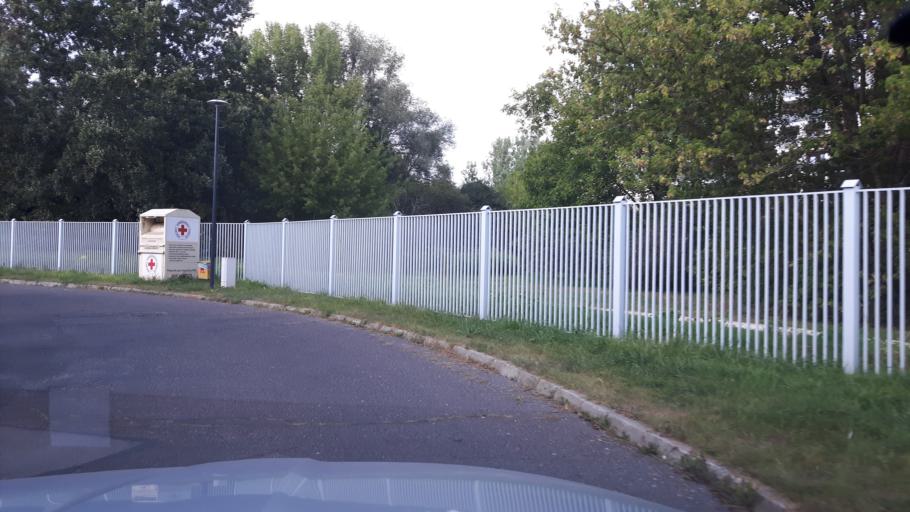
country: PL
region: Masovian Voivodeship
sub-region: Warszawa
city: Praga Poludnie
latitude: 52.2239
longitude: 21.0788
